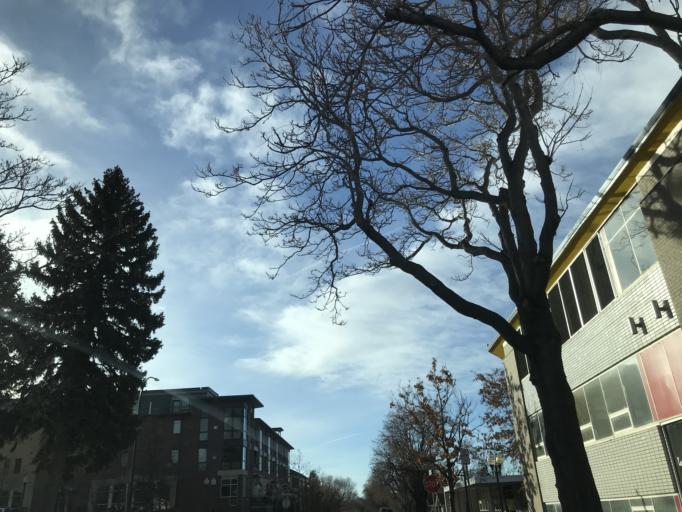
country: US
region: Colorado
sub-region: Arapahoe County
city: Littleton
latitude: 39.6137
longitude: -105.0115
